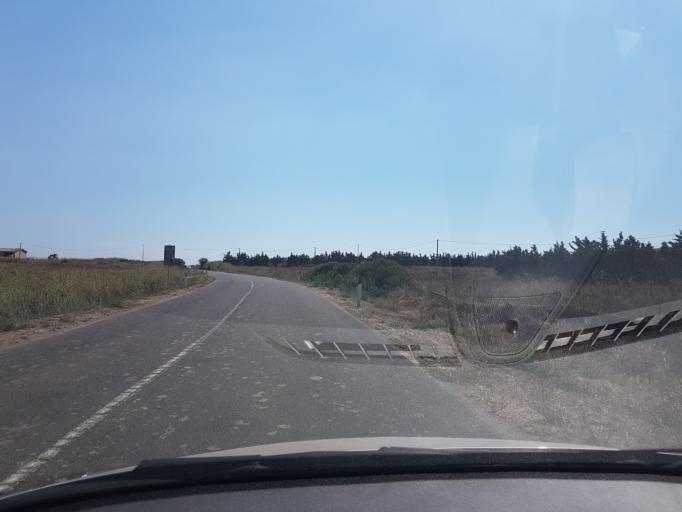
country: IT
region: Sardinia
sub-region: Provincia di Oristano
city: Nurachi
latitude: 39.9814
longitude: 8.4542
